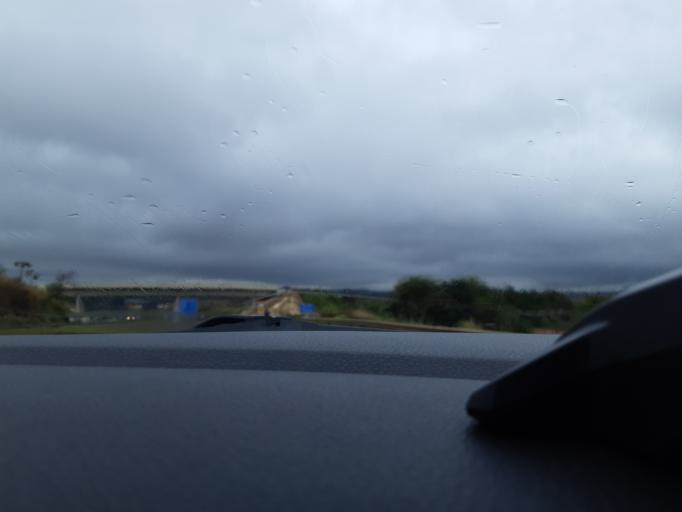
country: BR
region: Sao Paulo
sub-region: Ourinhos
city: Ourinhos
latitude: -23.0046
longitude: -49.9142
